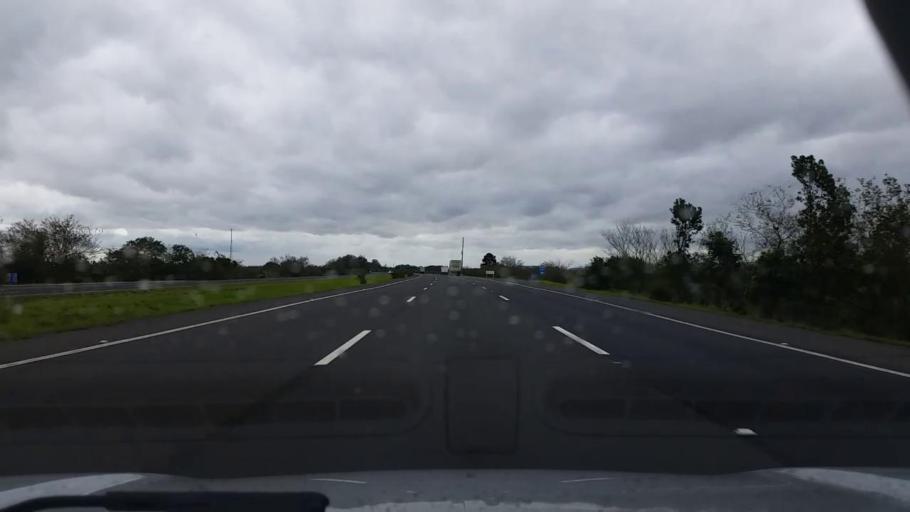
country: BR
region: Rio Grande do Sul
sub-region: Rolante
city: Rolante
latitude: -29.8862
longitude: -50.6571
